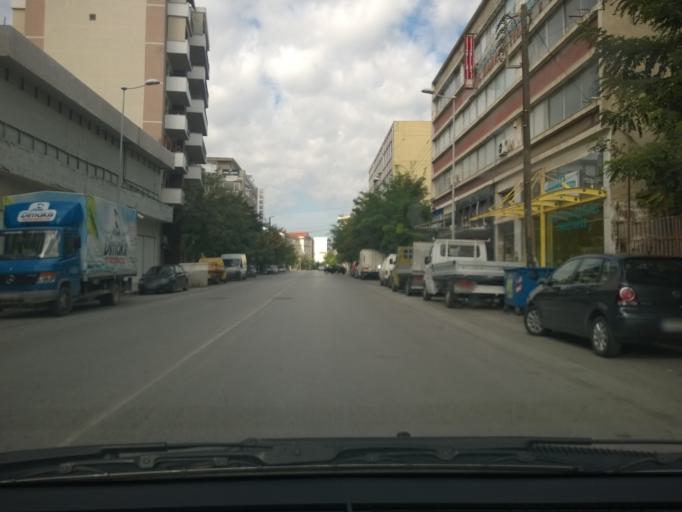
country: GR
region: Central Macedonia
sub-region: Nomos Thessalonikis
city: Ampelokipoi
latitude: 40.6481
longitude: 22.9188
